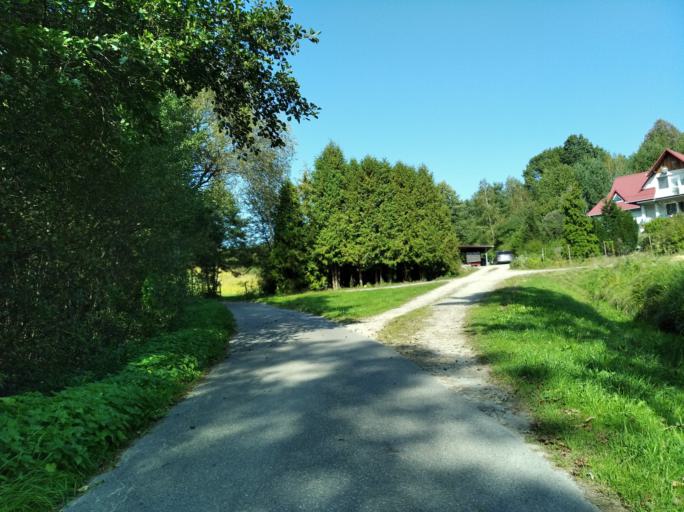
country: PL
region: Subcarpathian Voivodeship
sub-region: Powiat strzyzowski
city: Babica
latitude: 49.9374
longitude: 21.8605
